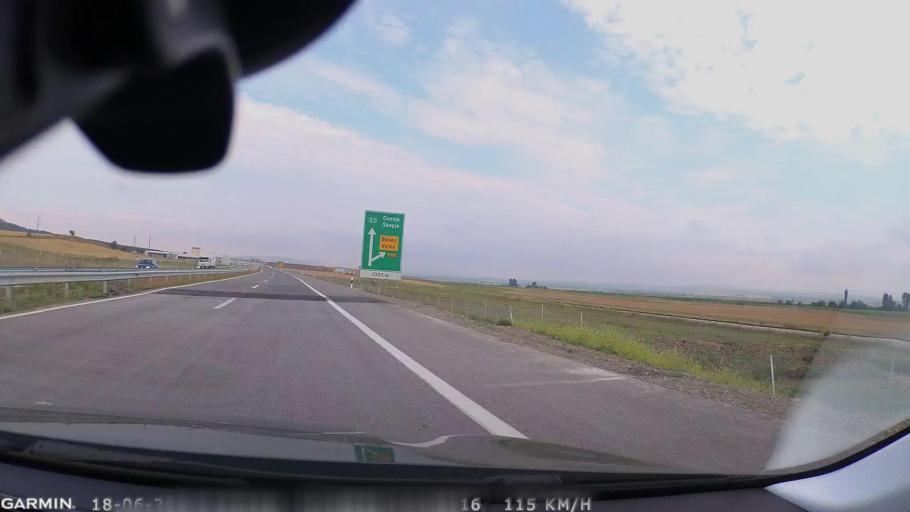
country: MK
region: Sveti Nikole
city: Sveti Nikole
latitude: 41.8093
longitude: 22.0544
